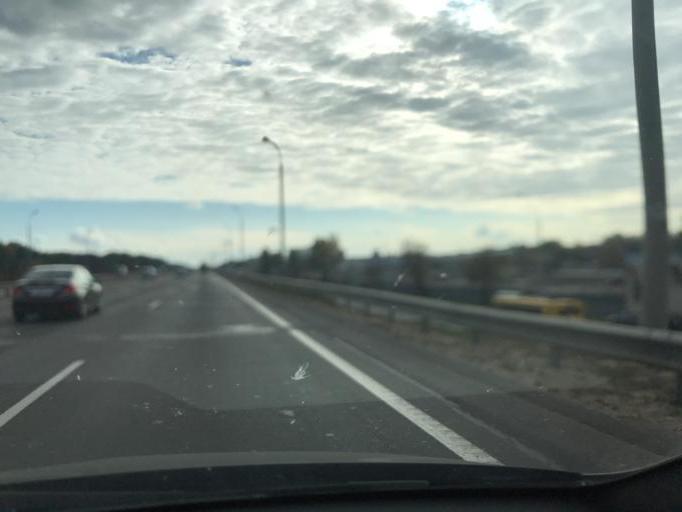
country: BY
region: Minsk
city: Vyaliki Trastsyanets
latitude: 53.9123
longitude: 27.6846
